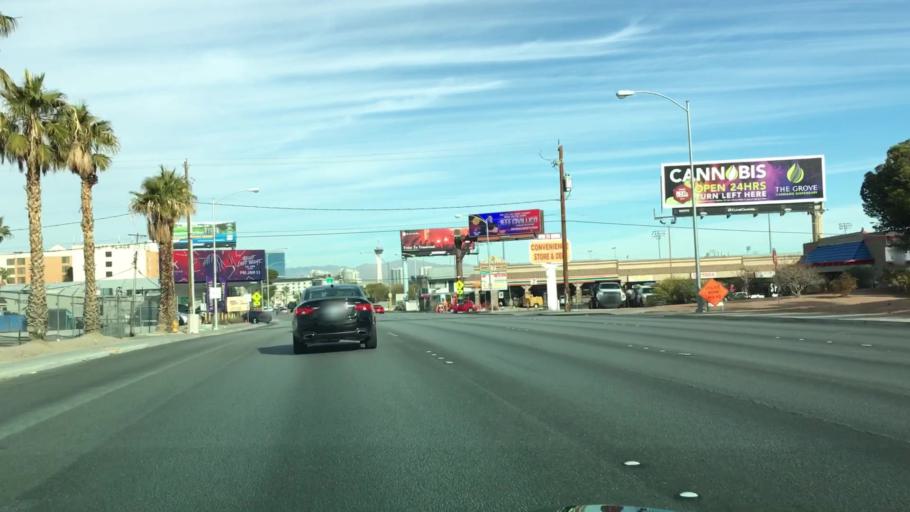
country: US
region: Nevada
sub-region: Clark County
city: Paradise
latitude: 36.1047
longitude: -115.1497
